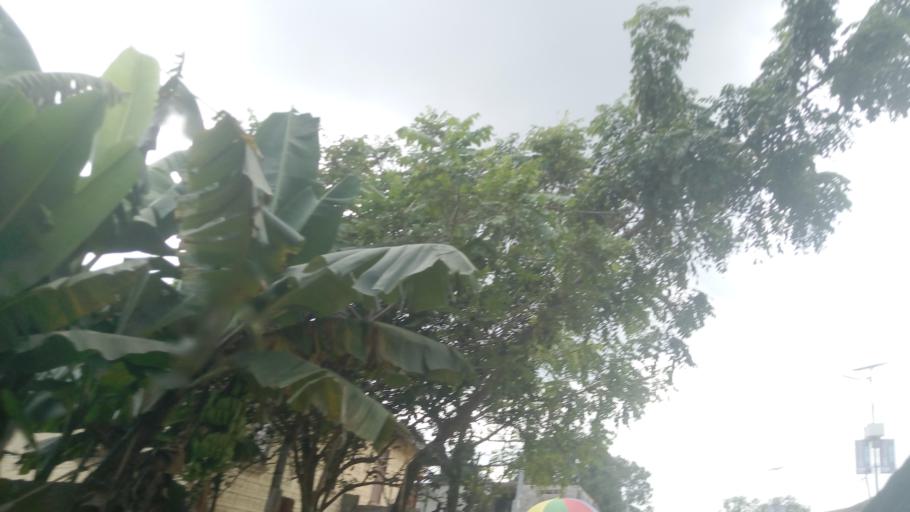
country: SL
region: Northern Province
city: Makeni
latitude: 8.8926
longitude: -12.0476
